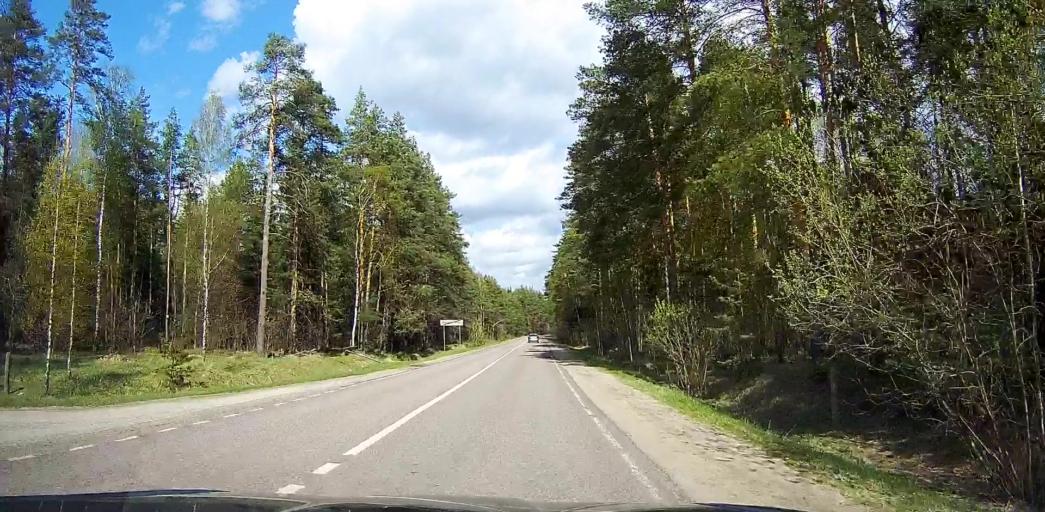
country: RU
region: Moskovskaya
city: Davydovo
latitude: 55.5632
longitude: 38.8143
